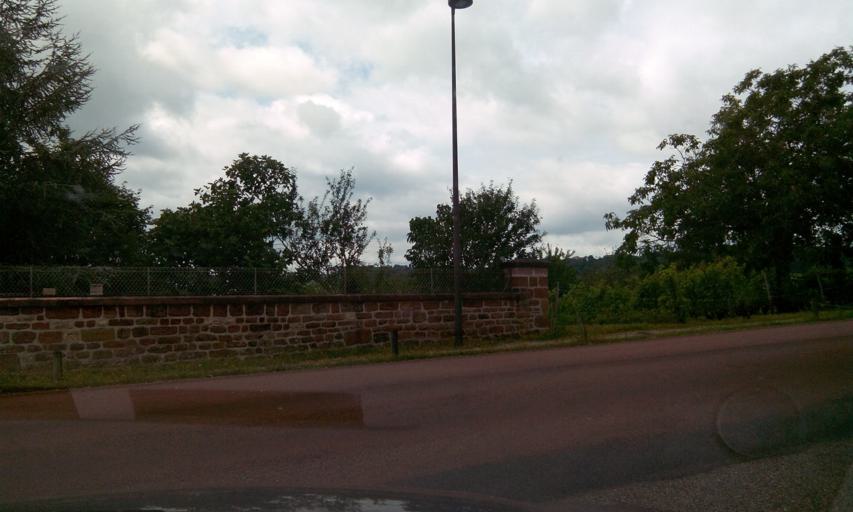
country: FR
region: Limousin
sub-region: Departement de la Correze
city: Meyssac
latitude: 45.0602
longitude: 1.6593
